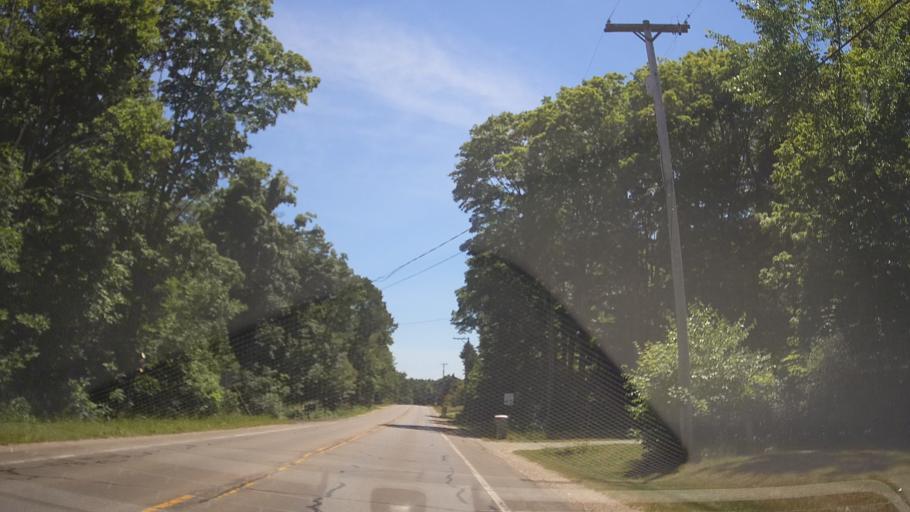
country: US
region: Michigan
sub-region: Grand Traverse County
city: Traverse City
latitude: 44.6907
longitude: -85.6905
